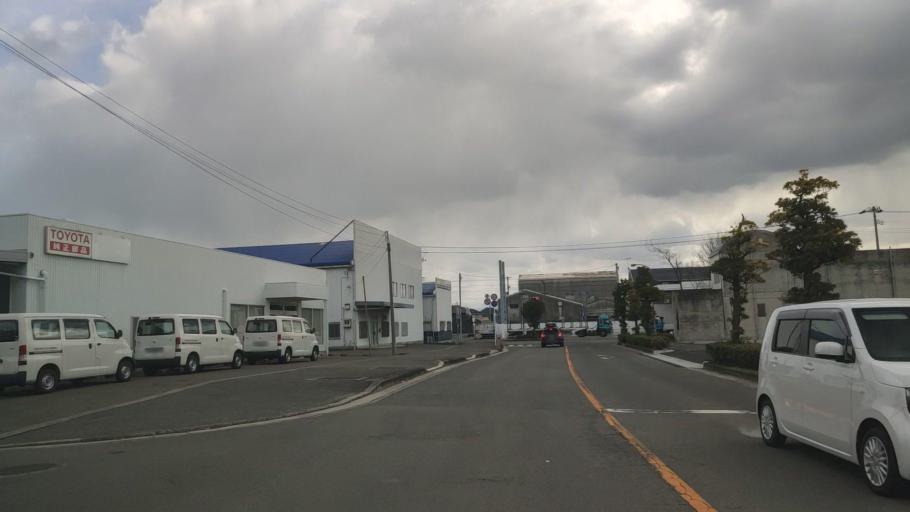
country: JP
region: Ehime
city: Saijo
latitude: 34.0571
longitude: 133.0182
